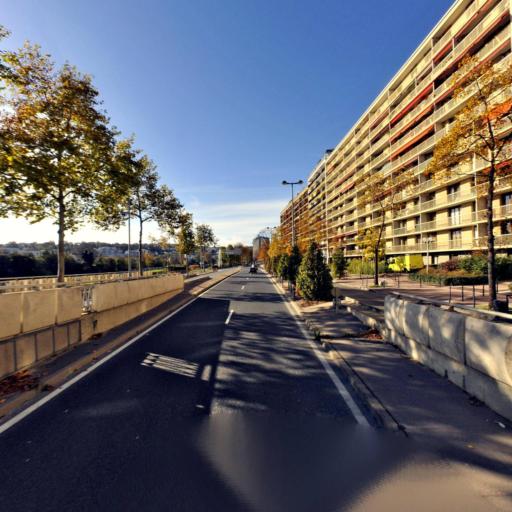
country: FR
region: Ile-de-France
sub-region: Departement des Hauts-de-Seine
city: Boulogne-Billancourt
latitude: 48.8247
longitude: 2.2471
